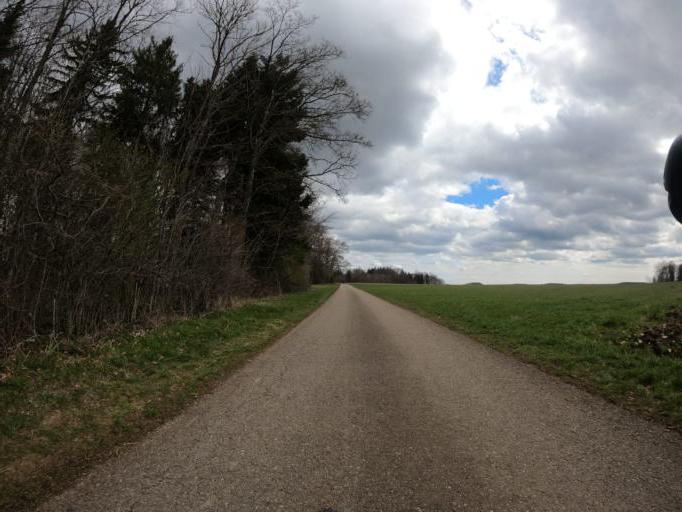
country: DE
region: Baden-Wuerttemberg
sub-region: Tuebingen Region
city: Jungingen
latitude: 48.3602
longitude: 9.0699
